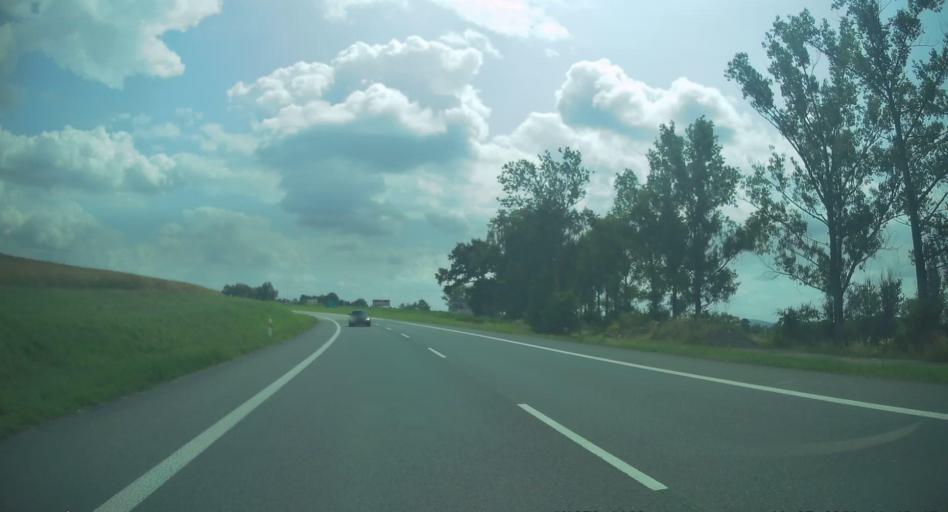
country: PL
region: Opole Voivodeship
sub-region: Powiat prudnicki
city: Prudnik
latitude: 50.3381
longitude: 17.5632
